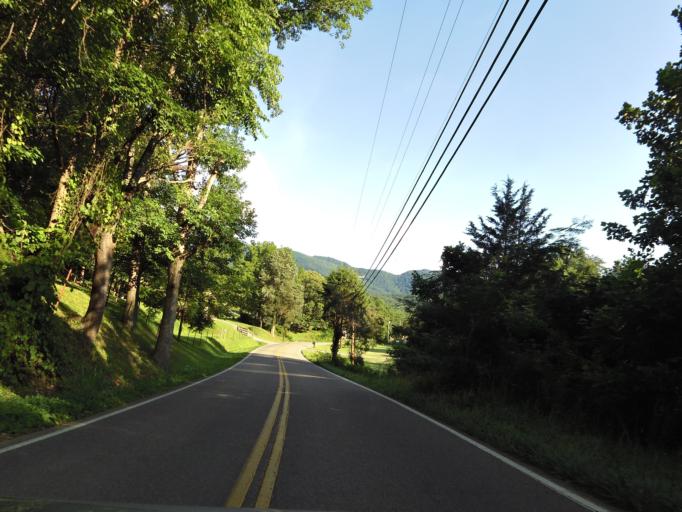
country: US
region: Tennessee
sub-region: Blount County
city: Maryville
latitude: 35.6632
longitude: -83.9627
